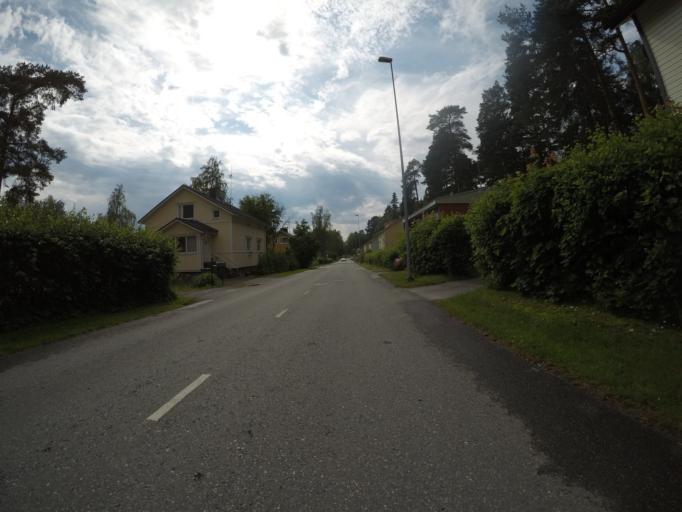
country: FI
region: Haeme
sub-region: Haemeenlinna
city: Haemeenlinna
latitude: 61.0125
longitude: 24.4694
